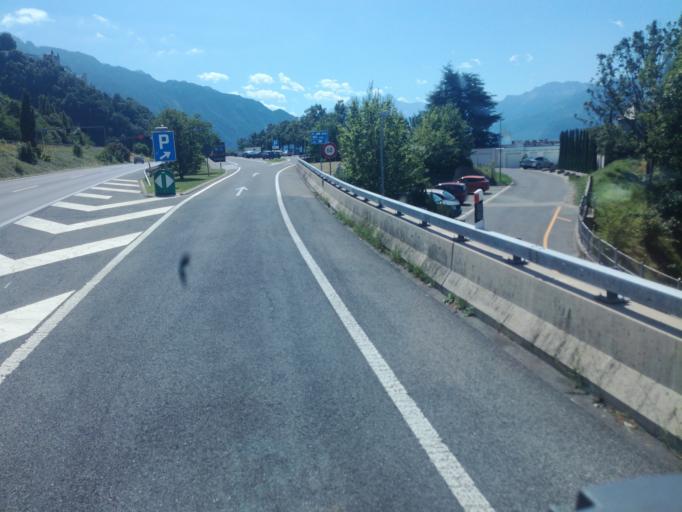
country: CH
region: Vaud
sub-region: Riviera-Pays-d'Enhaut District
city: Montreux
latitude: 46.4392
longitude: 6.9156
